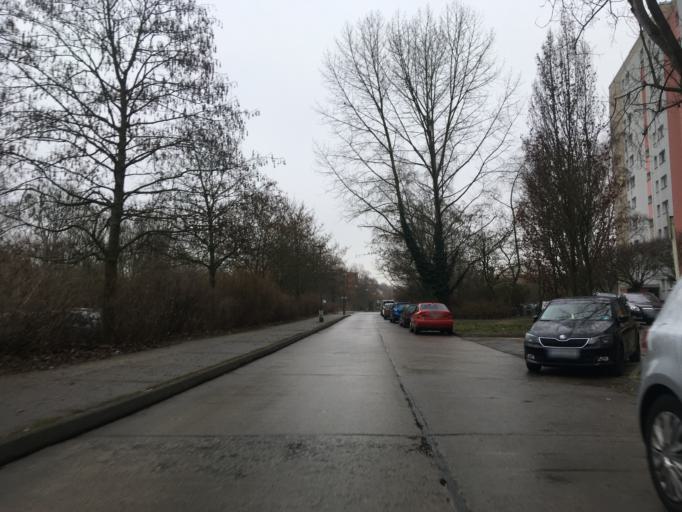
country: DE
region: Berlin
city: Buch
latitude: 52.6292
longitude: 13.4950
